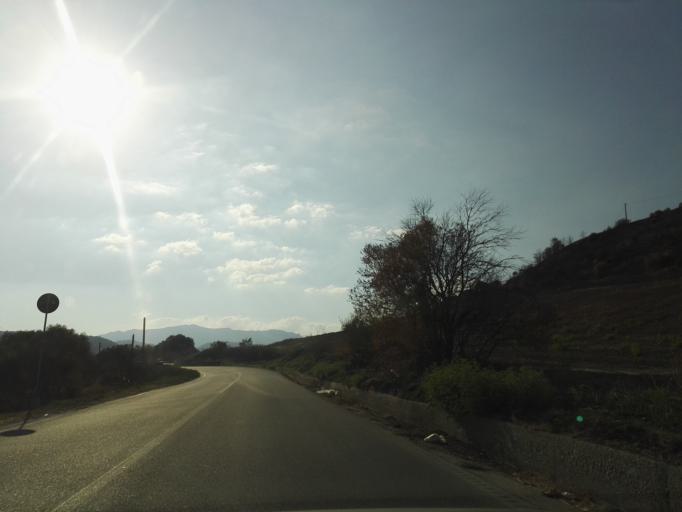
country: IT
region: Calabria
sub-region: Provincia di Reggio Calabria
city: Monasterace
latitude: 38.4390
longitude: 16.5495
